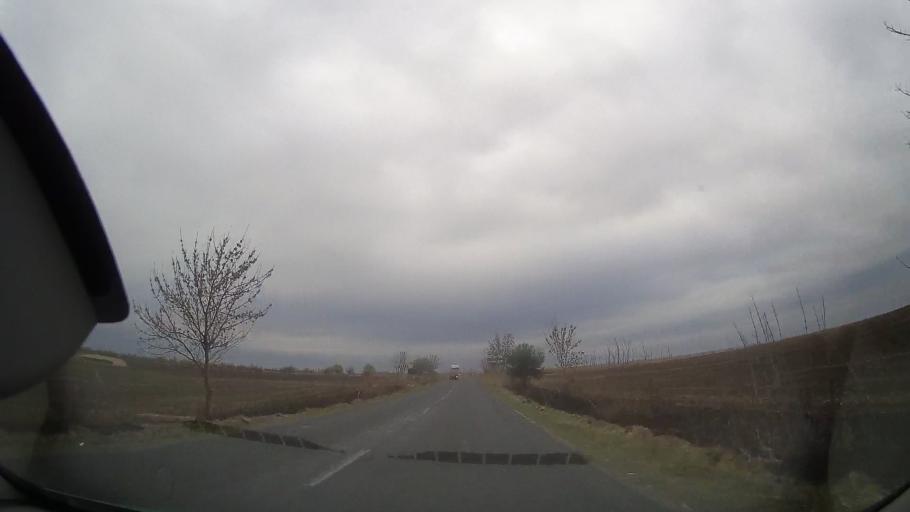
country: RO
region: Buzau
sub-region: Comuna Padina
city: Padina
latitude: 44.7816
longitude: 27.1514
